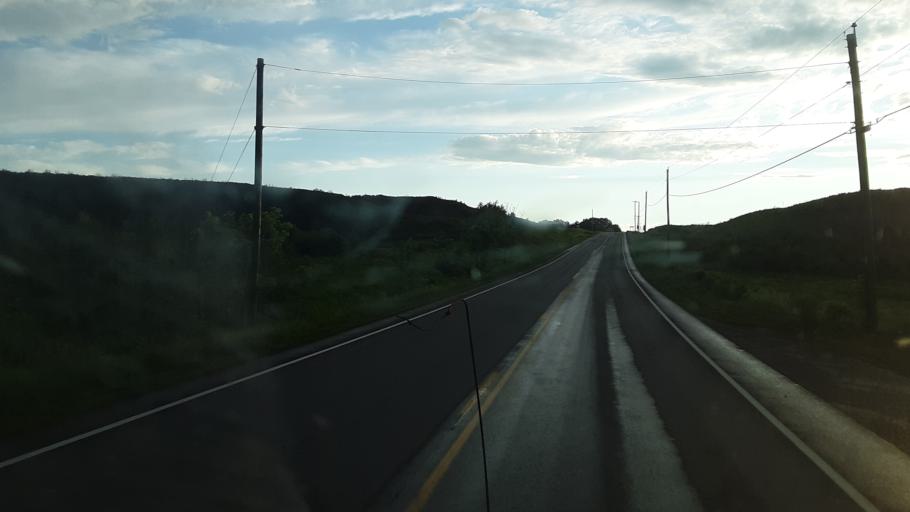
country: US
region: Maine
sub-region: Aroostook County
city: Presque Isle
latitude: 46.6749
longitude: -67.9689
